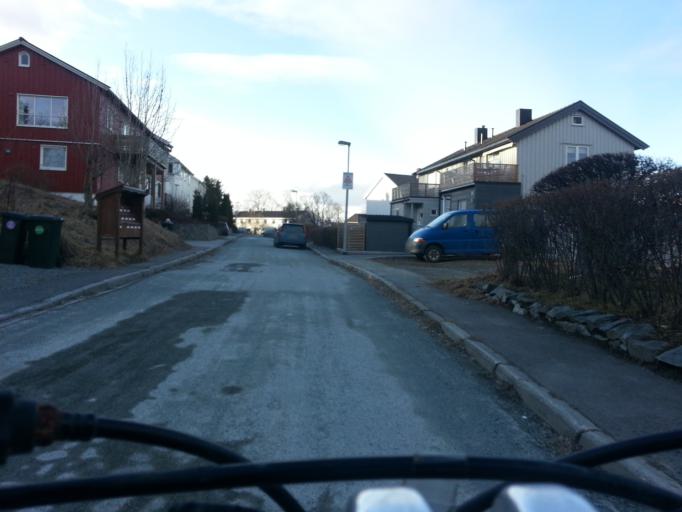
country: NO
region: Sor-Trondelag
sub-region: Trondheim
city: Trondheim
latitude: 63.4464
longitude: 10.4621
